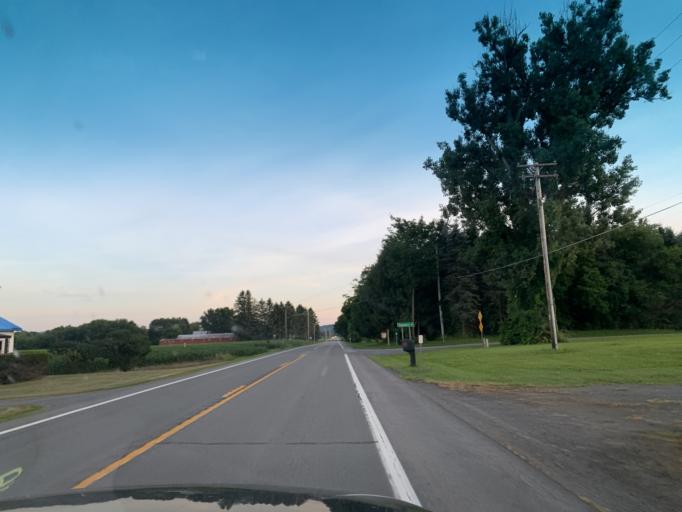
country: US
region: New York
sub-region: Oneida County
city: Chadwicks
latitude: 42.9060
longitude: -75.2414
